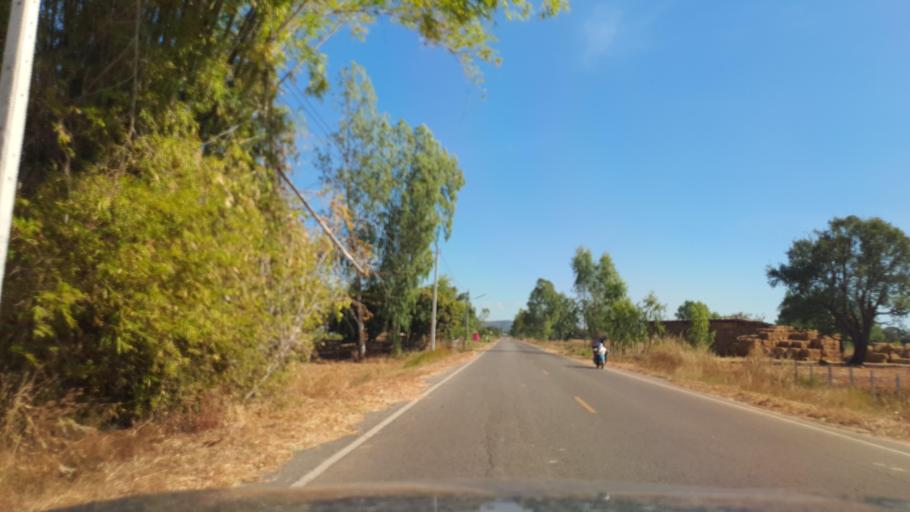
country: TH
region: Kalasin
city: Khao Wong
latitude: 16.7214
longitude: 104.1070
